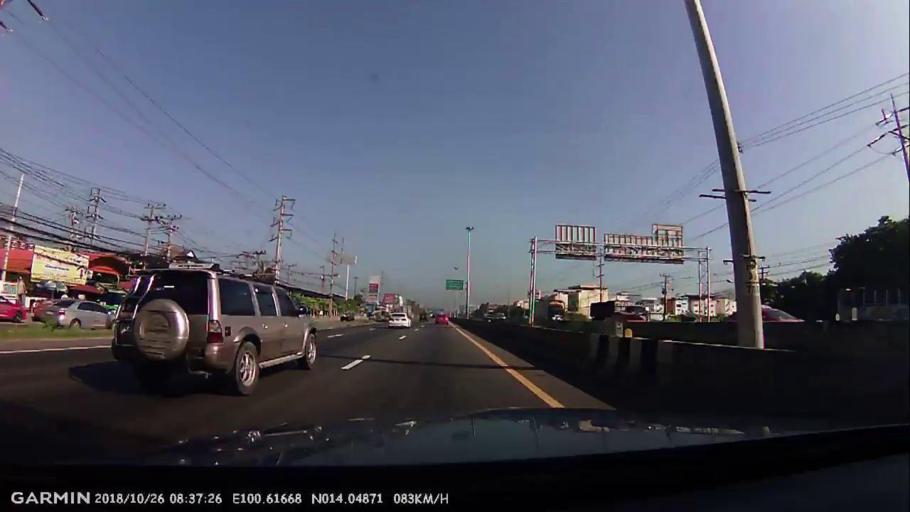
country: TH
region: Pathum Thani
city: Khlong Luang
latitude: 14.0490
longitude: 100.6166
